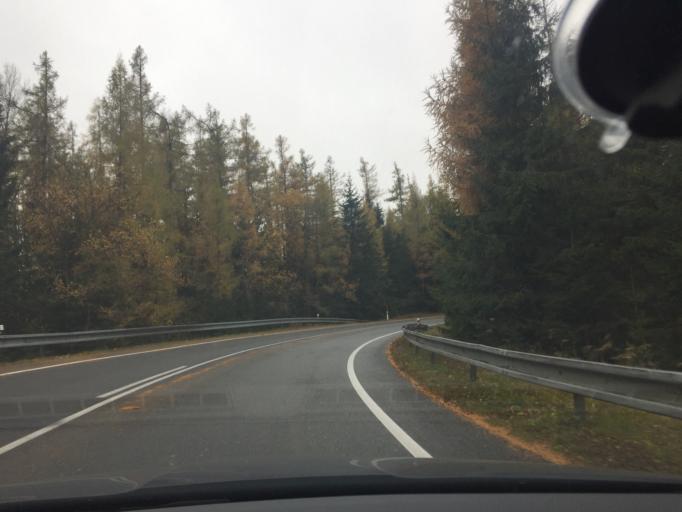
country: SK
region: Presovsky
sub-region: Okres Poprad
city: Strba
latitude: 49.1113
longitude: 20.0777
